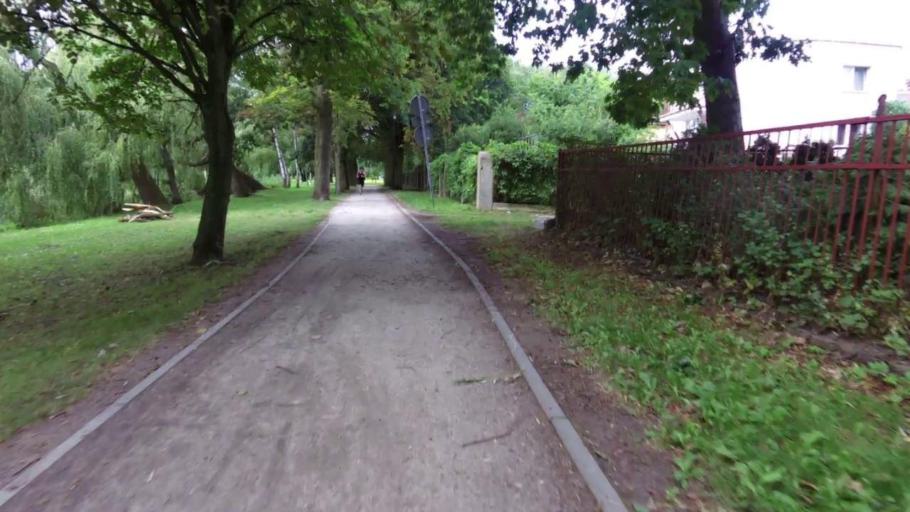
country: PL
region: West Pomeranian Voivodeship
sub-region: Powiat choszczenski
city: Choszczno
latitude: 53.1638
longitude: 15.4199
